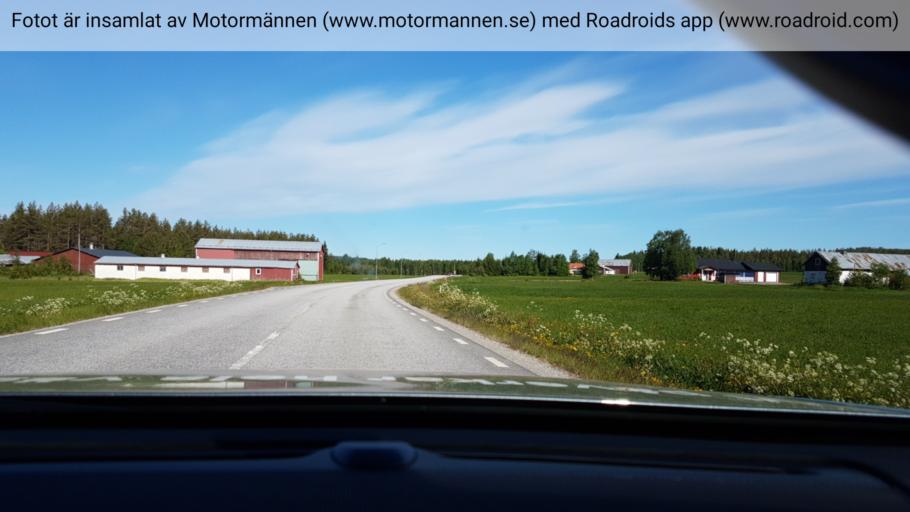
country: SE
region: Vaesterbotten
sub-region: Vindelns Kommun
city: Vindeln
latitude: 64.1049
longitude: 19.5955
